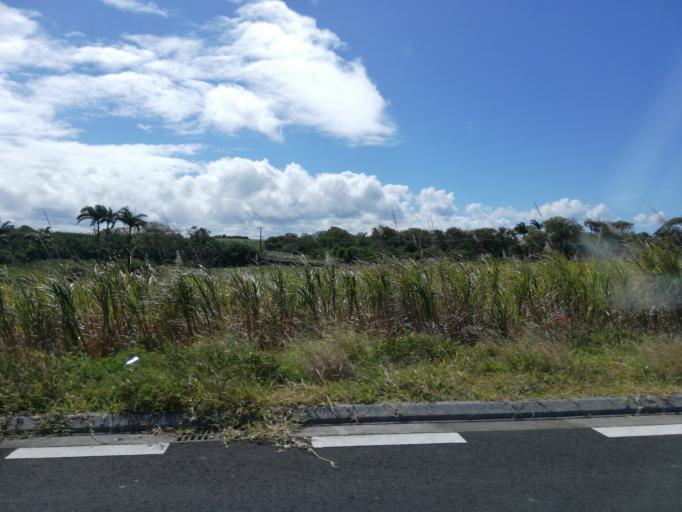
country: MU
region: Grand Port
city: Beau Vallon
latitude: -20.4503
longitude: 57.6944
